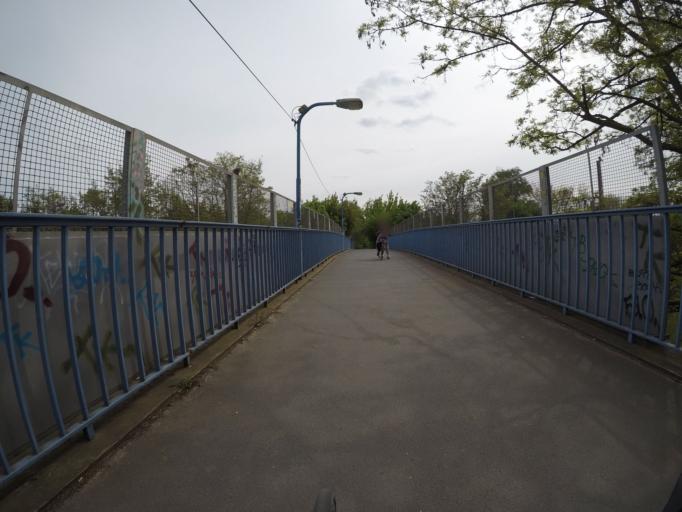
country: DE
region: Berlin
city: Altglienicke
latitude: 52.4034
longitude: 13.5379
